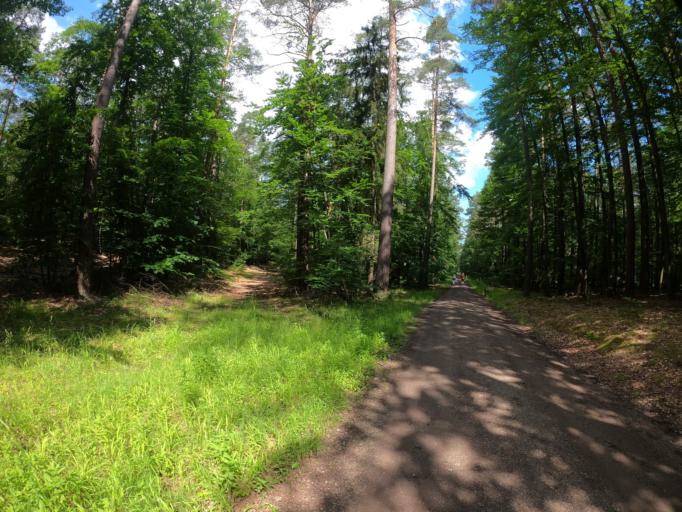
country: DE
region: Bavaria
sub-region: Upper Franconia
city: Memmelsdorf
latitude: 49.8927
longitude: 10.9518
